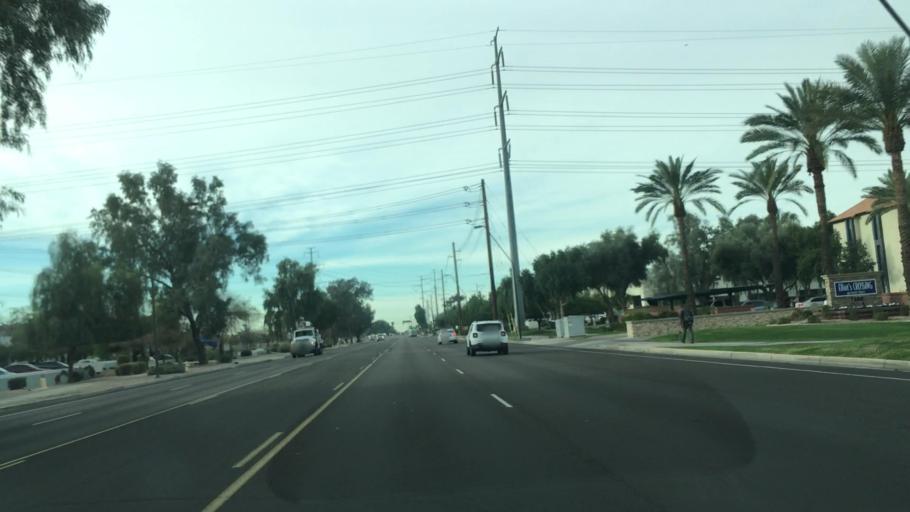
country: US
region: Arizona
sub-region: Maricopa County
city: Guadalupe
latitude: 33.3540
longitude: -111.9459
